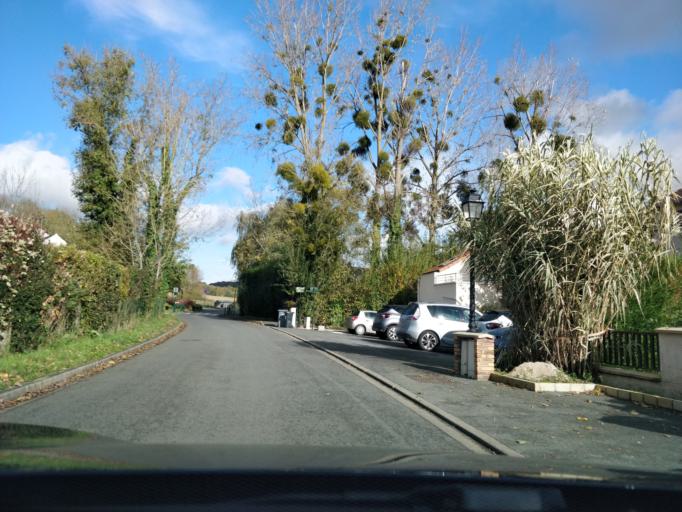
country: FR
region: Ile-de-France
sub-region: Departement de l'Essonne
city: Fontenay-les-Briis
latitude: 48.6219
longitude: 2.1591
